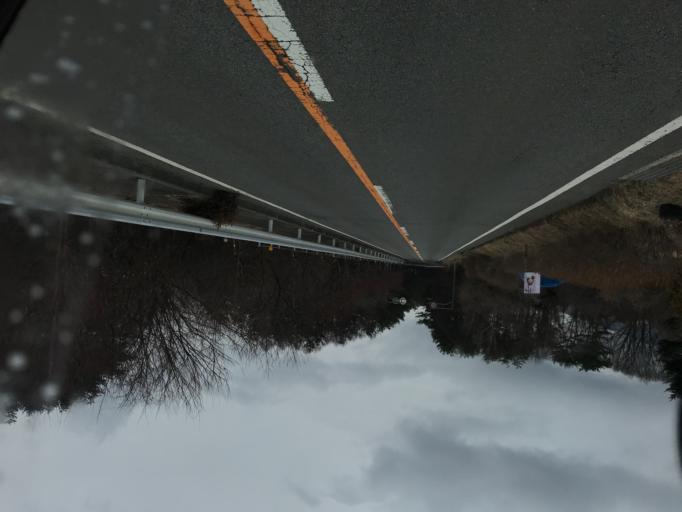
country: JP
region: Nagano
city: Chino
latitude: 35.8875
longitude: 138.3212
